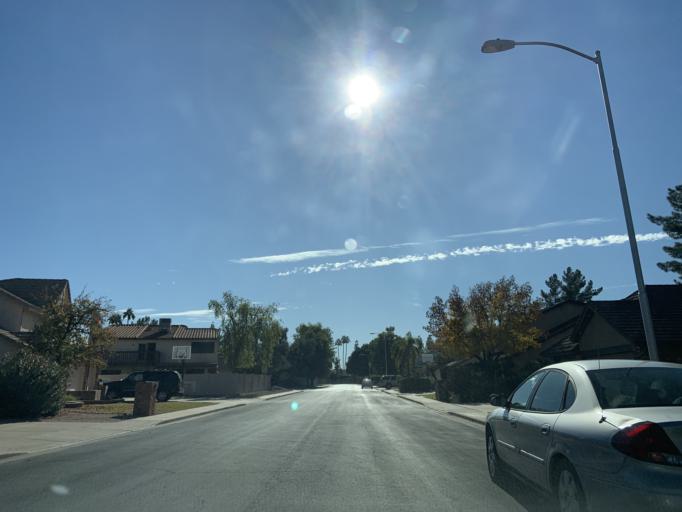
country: US
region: Arizona
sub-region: Maricopa County
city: San Carlos
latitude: 33.3683
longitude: -111.8802
